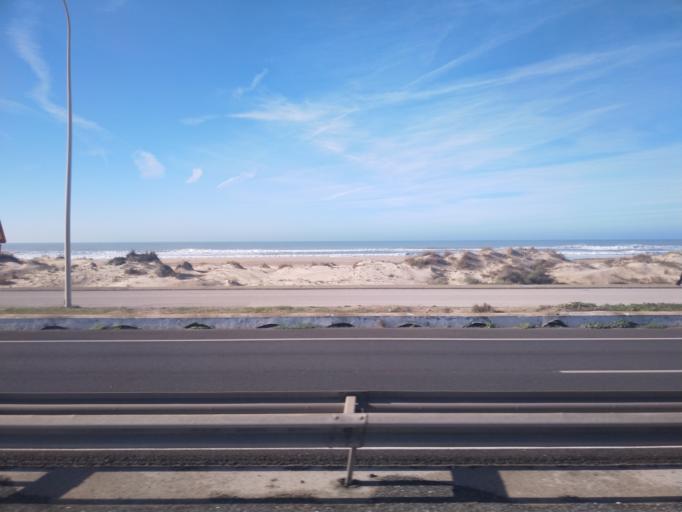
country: ES
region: Andalusia
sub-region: Provincia de Cadiz
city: Cadiz
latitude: 36.4825
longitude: -6.2634
